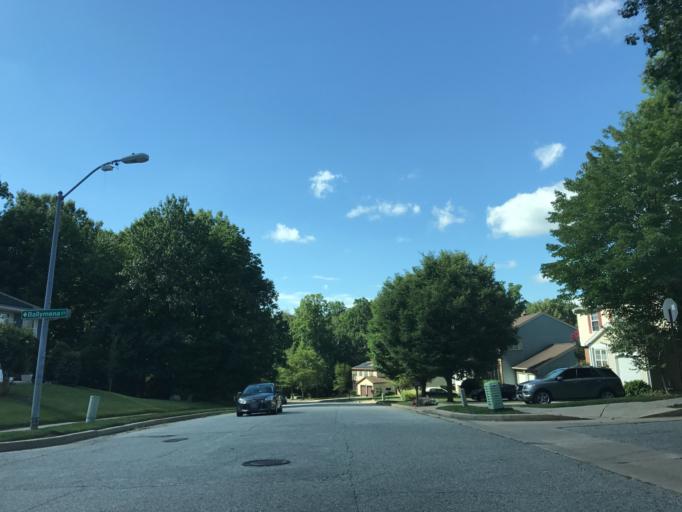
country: US
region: Maryland
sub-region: Howard County
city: Ellicott City
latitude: 39.2998
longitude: -76.7714
